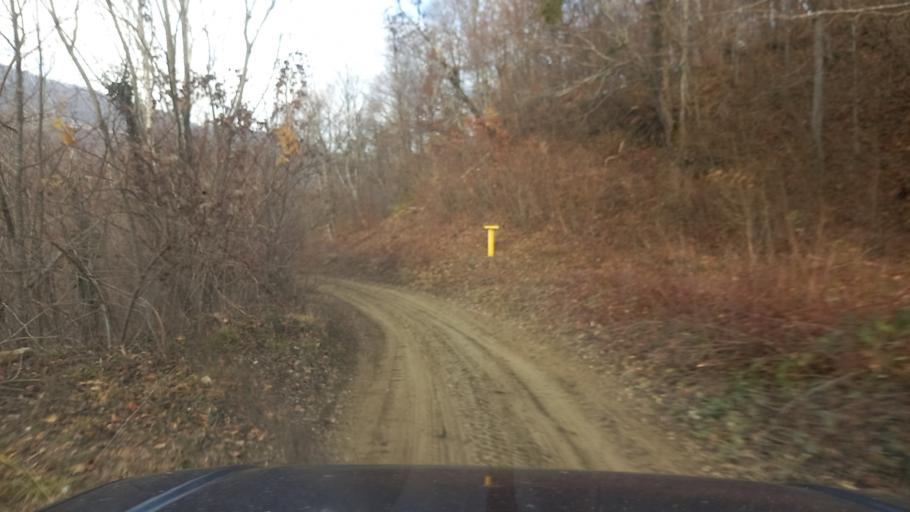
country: RU
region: Krasnodarskiy
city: Neftegorsk
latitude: 44.2085
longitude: 39.7096
